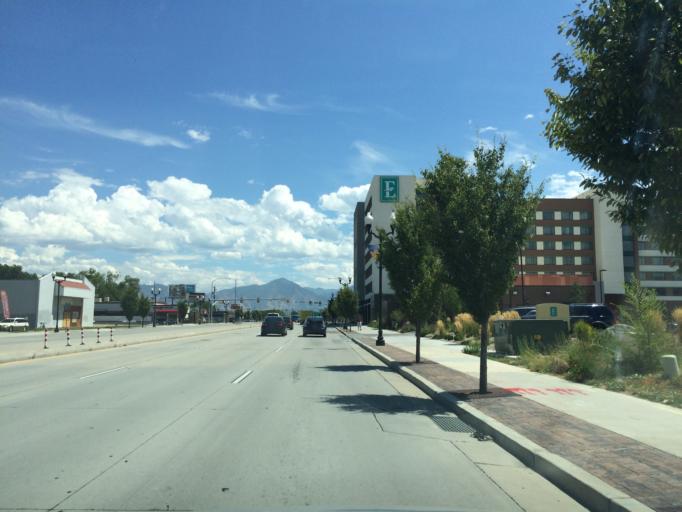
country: US
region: Utah
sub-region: Salt Lake County
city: Taylorsville
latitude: 40.6965
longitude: -111.9625
